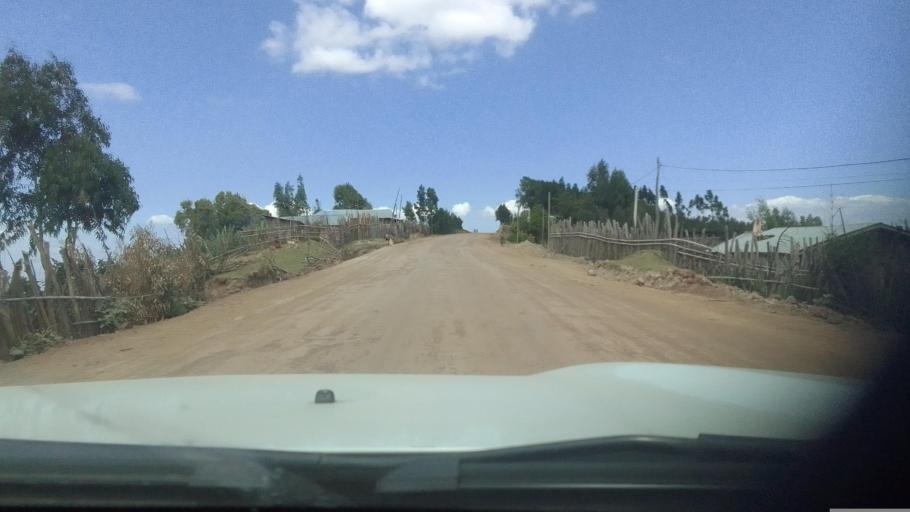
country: ET
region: Oromiya
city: Hagere Hiywet
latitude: 8.8399
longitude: 37.8857
